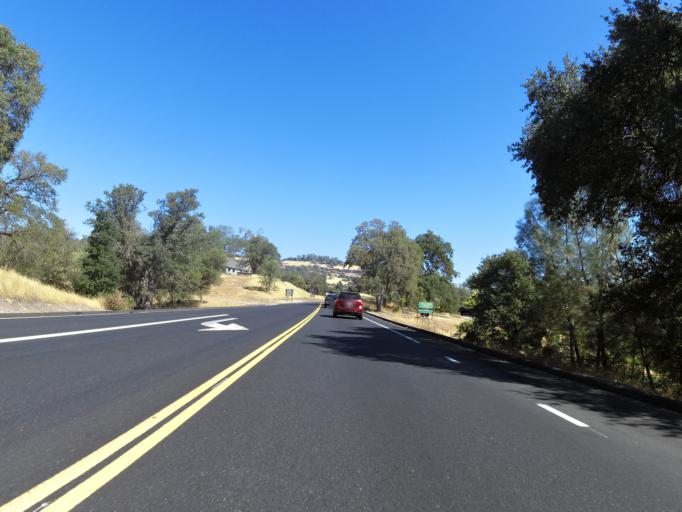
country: US
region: California
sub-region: Calaveras County
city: Murphys
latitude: 38.0954
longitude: -120.4716
